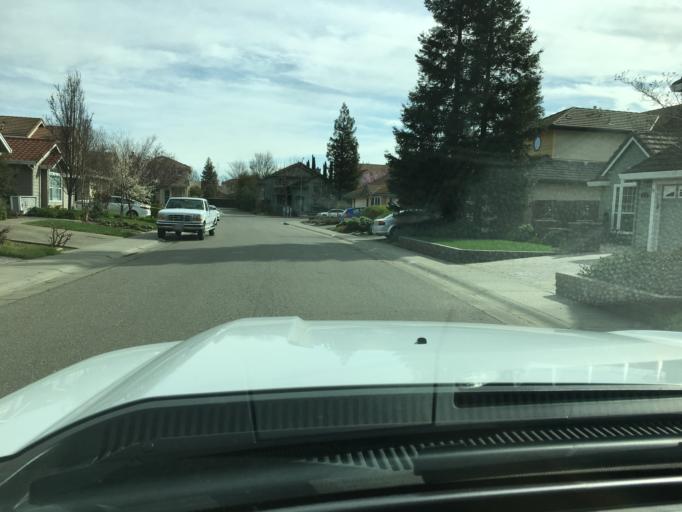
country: US
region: California
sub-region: Yolo County
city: Davis
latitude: 38.5580
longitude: -121.7772
